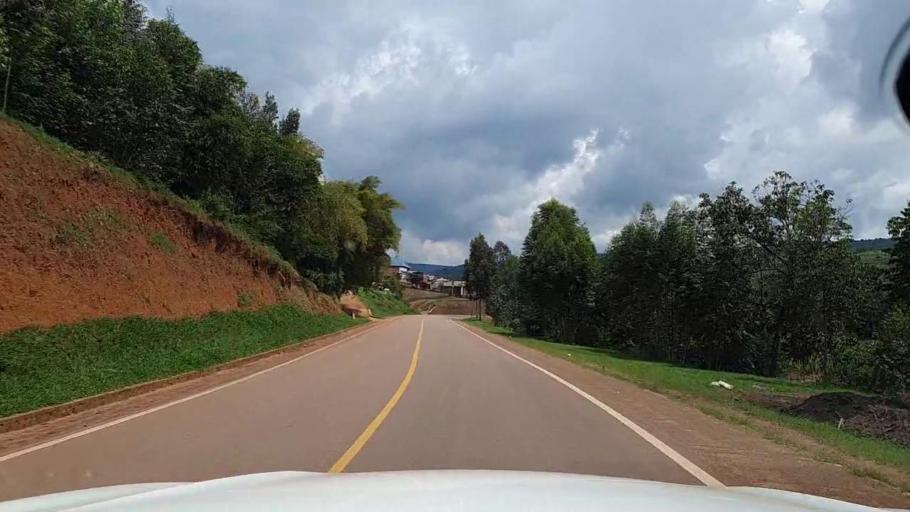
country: RW
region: Kigali
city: Kigali
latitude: -1.8093
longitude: 30.1241
